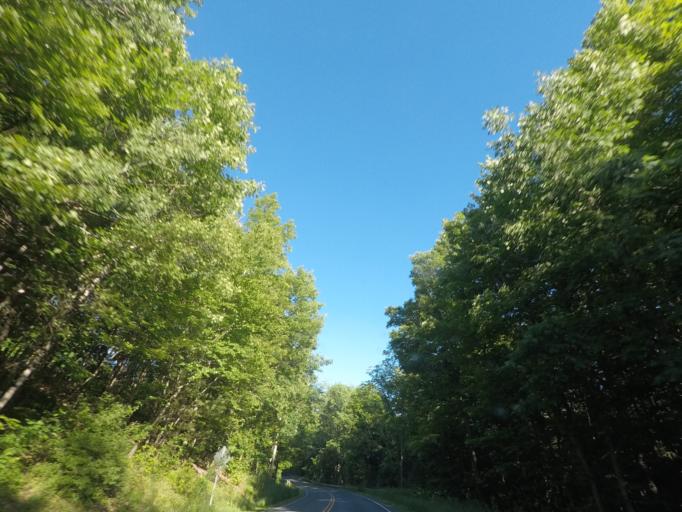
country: US
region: New York
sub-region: Rensselaer County
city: West Sand Lake
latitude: 42.5943
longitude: -73.5910
